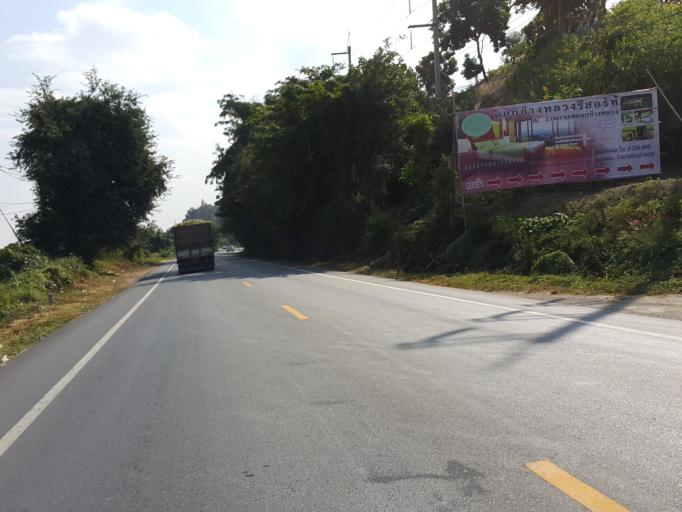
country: TH
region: Lamphun
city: Ban Hong
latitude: 18.2858
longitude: 98.8175
